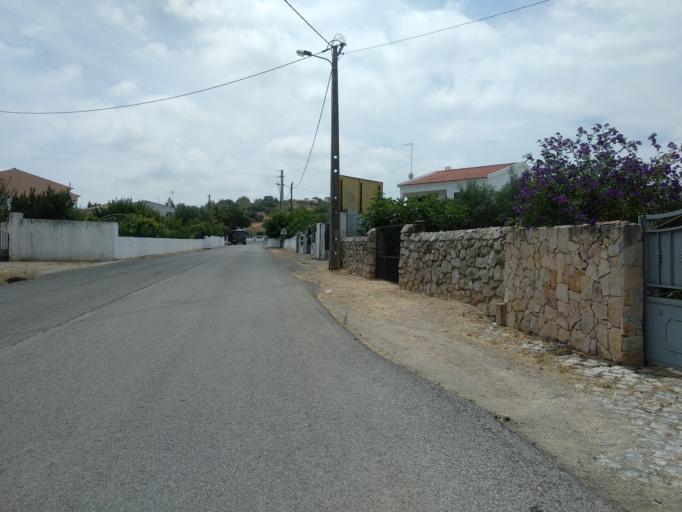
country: PT
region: Faro
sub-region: Sao Bras de Alportel
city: Sao Bras de Alportel
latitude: 37.1670
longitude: -7.8914
